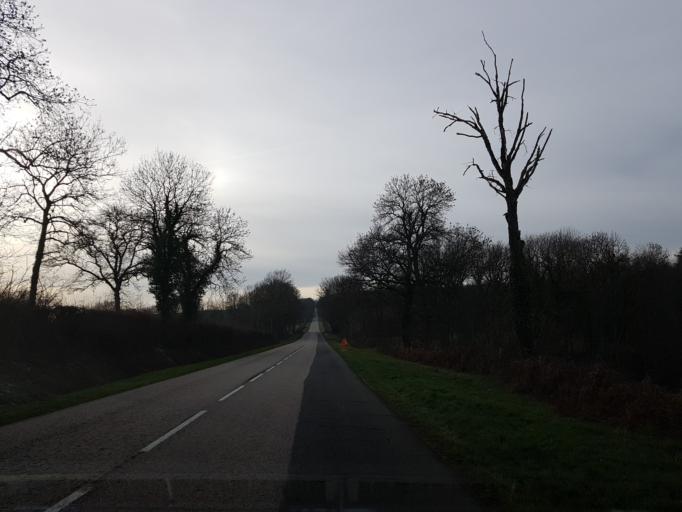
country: FR
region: Auvergne
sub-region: Departement de l'Allier
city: Souvigny
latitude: 46.4398
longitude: 3.0963
